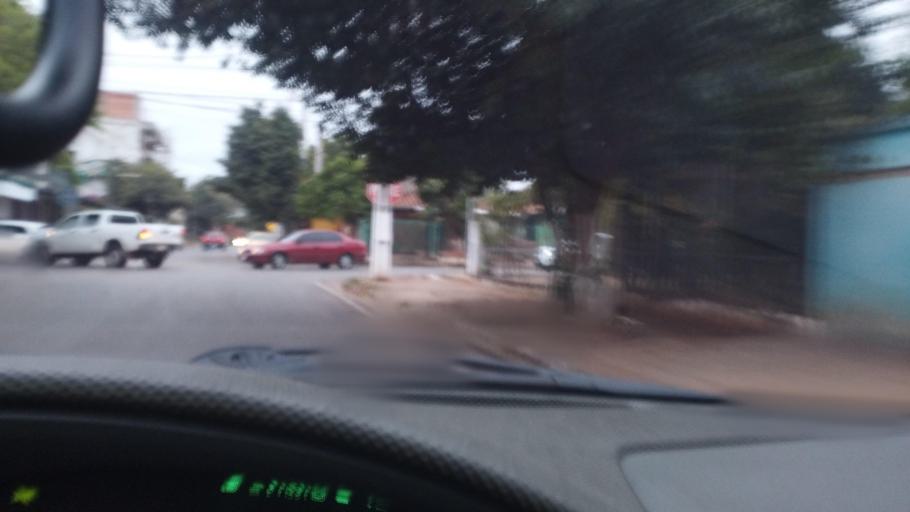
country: PY
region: Central
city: Fernando de la Mora
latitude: -25.2998
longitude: -57.5290
